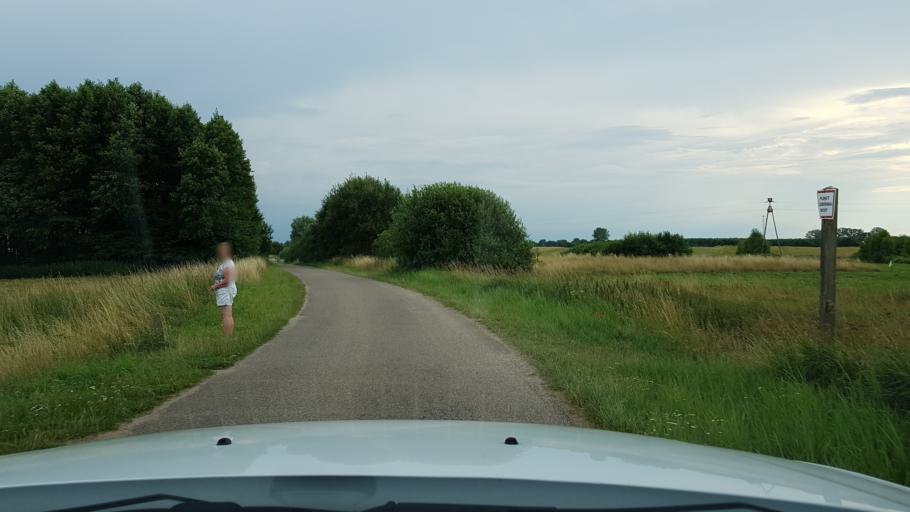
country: PL
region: West Pomeranian Voivodeship
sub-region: Powiat drawski
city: Wierzchowo
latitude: 53.4716
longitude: 16.1215
